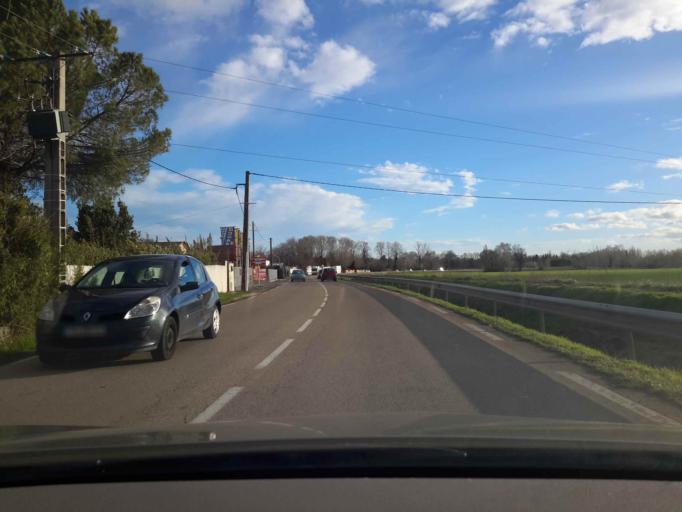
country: FR
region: Languedoc-Roussillon
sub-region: Departement du Gard
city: Caissargues
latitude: 43.7966
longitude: 4.3524
